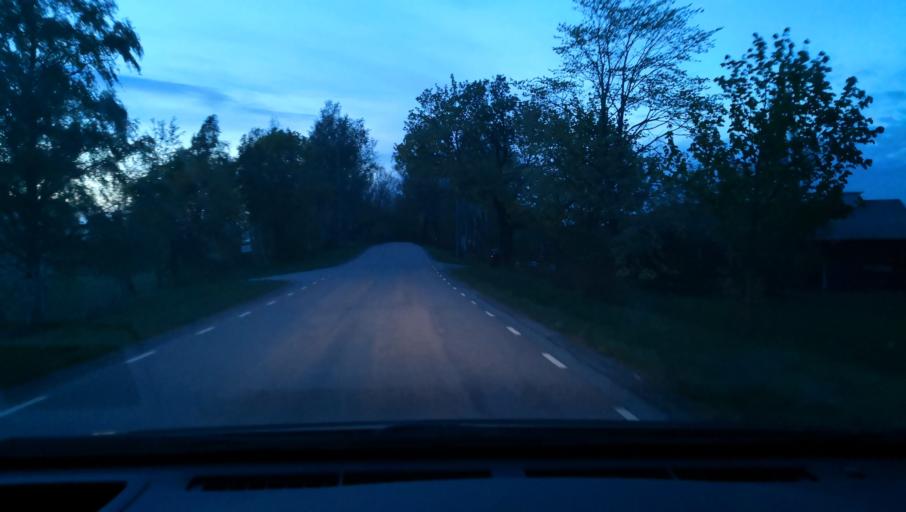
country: SE
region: OErebro
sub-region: Askersunds Kommun
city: Asbro
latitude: 59.0818
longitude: 15.0063
